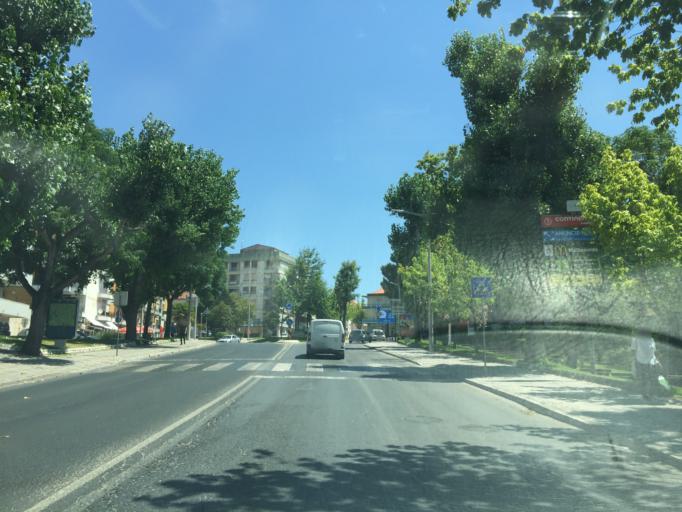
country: PT
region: Santarem
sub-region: Tomar
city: Tomar
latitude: 39.6030
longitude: -8.4101
